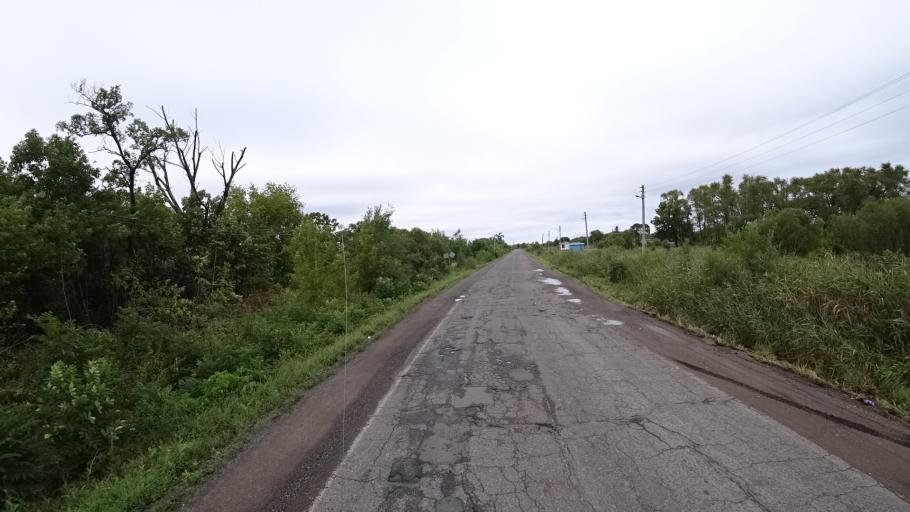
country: RU
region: Primorskiy
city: Monastyrishche
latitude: 44.1904
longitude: 132.4816
